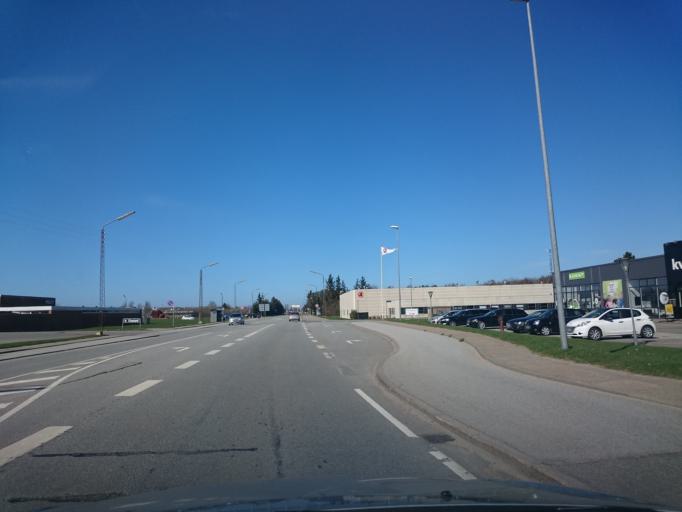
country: DK
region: North Denmark
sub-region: Hjorring Kommune
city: Hjorring
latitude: 57.4566
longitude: 10.0178
